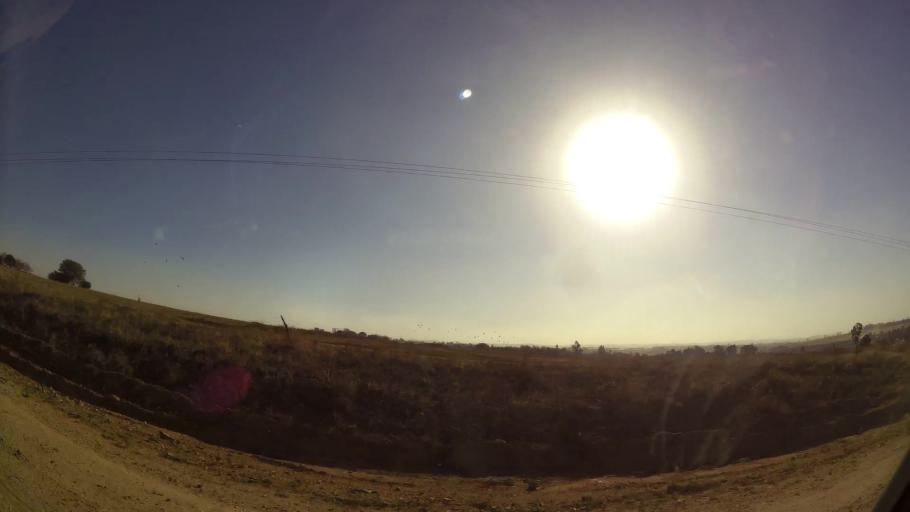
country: ZA
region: Gauteng
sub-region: City of Johannesburg Metropolitan Municipality
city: Diepsloot
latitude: -25.9573
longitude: 27.9584
